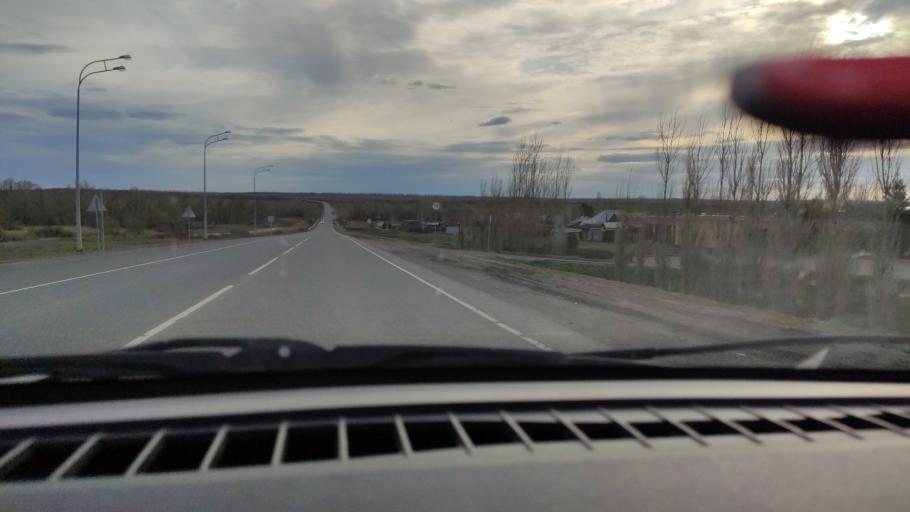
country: RU
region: Orenburg
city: Tatarskaya Kargala
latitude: 52.0258
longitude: 55.2270
